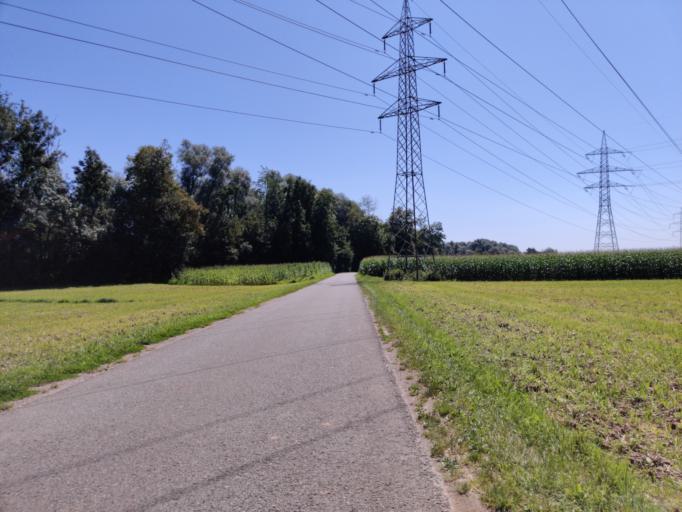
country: AT
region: Styria
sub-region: Politischer Bezirk Leibnitz
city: Ragnitz
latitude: 46.8356
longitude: 15.5528
